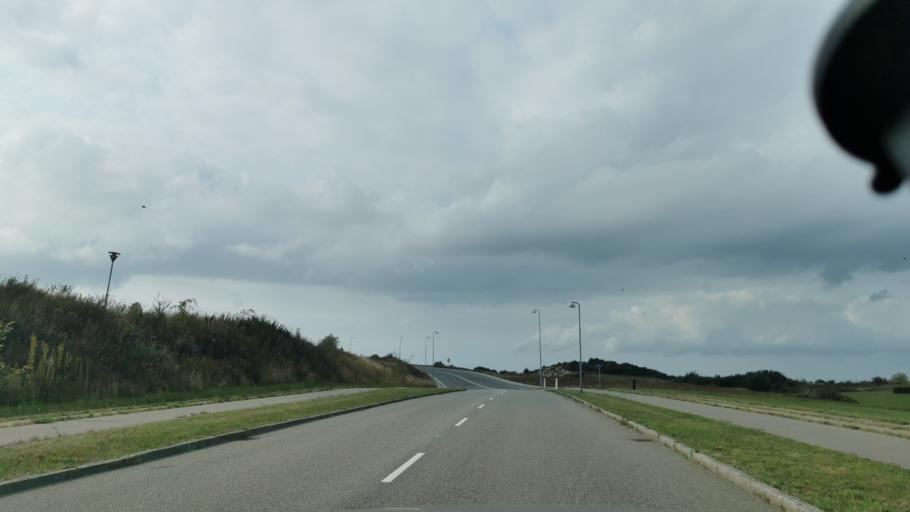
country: DK
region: Zealand
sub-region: Kalundborg Kommune
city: Kalundborg
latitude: 55.6929
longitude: 11.0836
